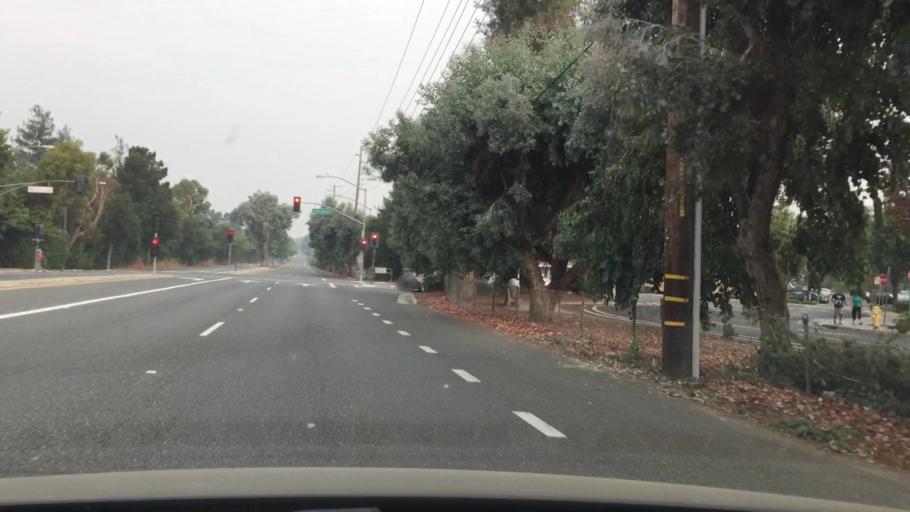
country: US
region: California
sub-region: Santa Clara County
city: Loyola
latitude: 37.3409
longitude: -122.0718
